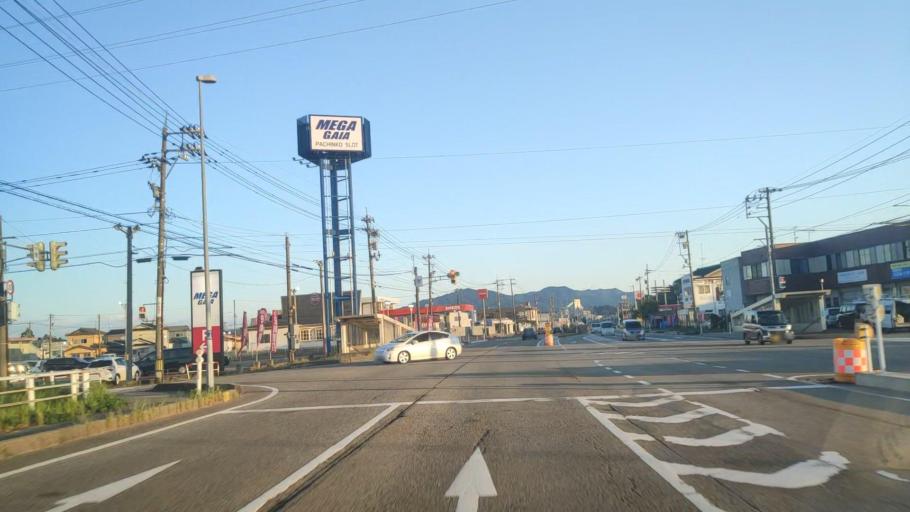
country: JP
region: Toyama
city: Himi
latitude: 36.8354
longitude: 136.9901
